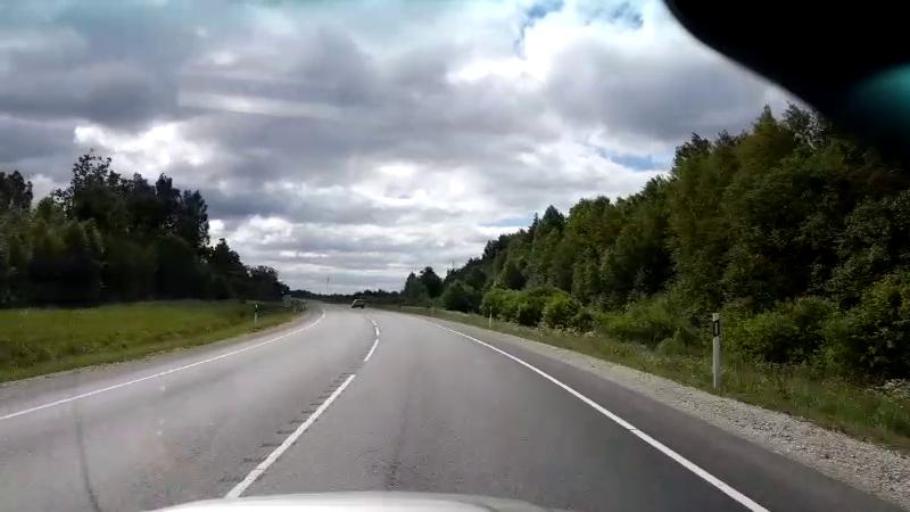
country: EE
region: Paernumaa
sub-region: Halinga vald
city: Parnu-Jaagupi
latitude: 58.6719
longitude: 24.4474
